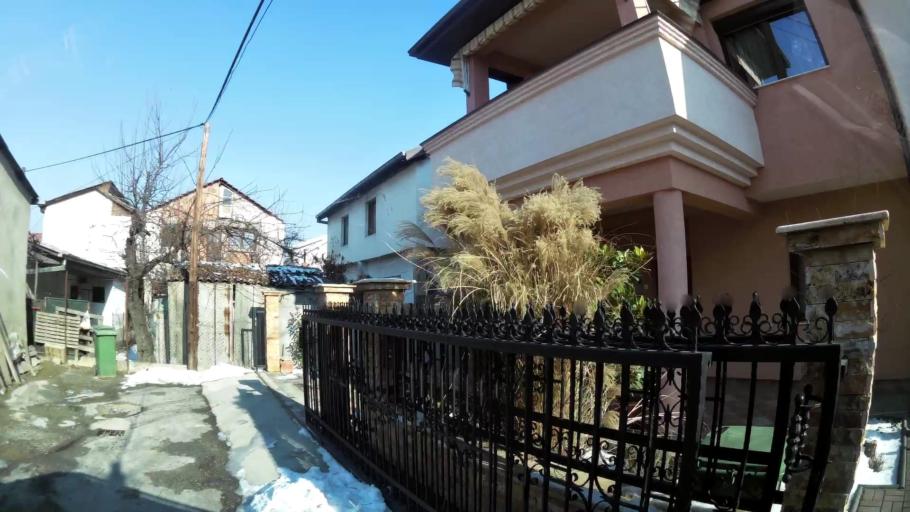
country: MK
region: Kisela Voda
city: Usje
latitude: 41.9718
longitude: 21.4498
